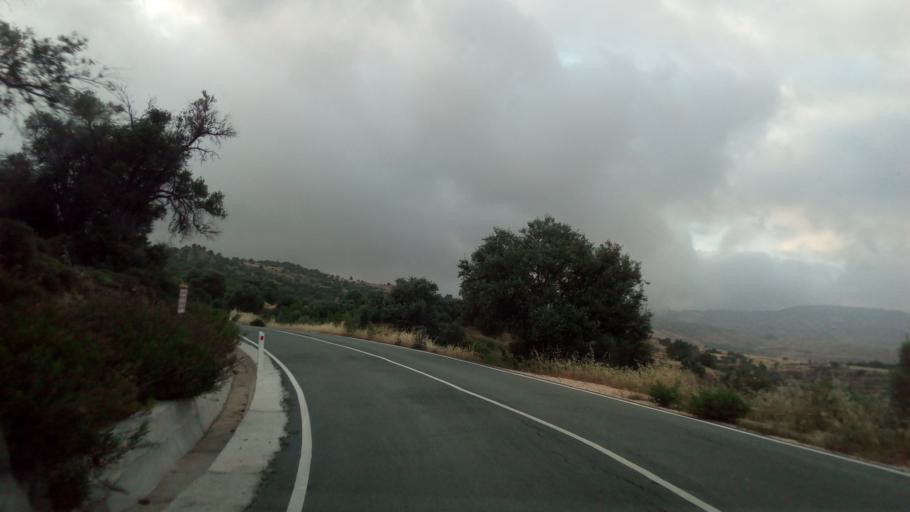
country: CY
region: Limassol
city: Pachna
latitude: 34.8559
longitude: 32.6453
